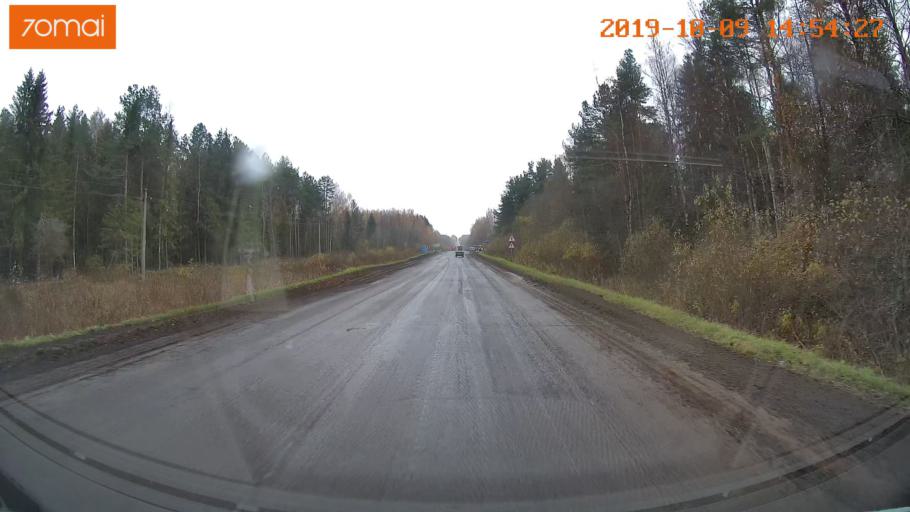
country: RU
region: Kostroma
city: Chistyye Bory
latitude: 58.3566
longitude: 41.6428
